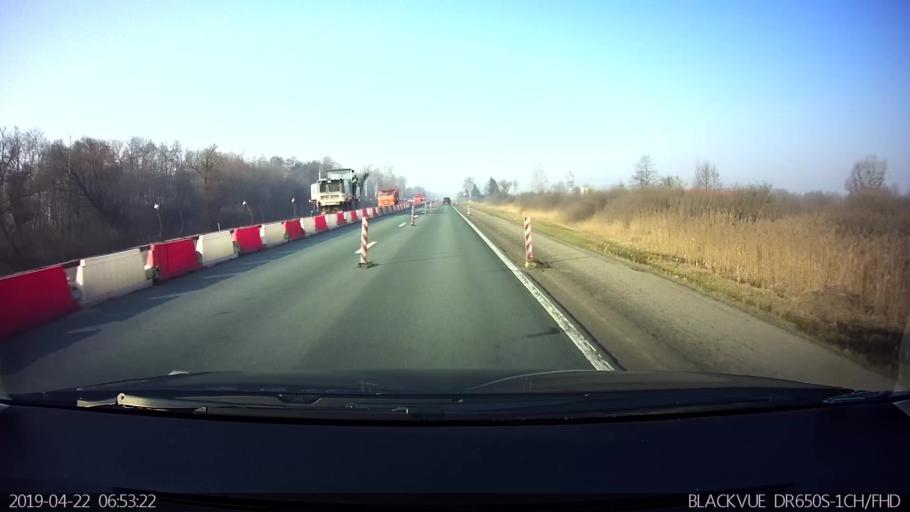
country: RU
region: Smolensk
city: Gagarin
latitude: 55.4779
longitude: 34.9267
